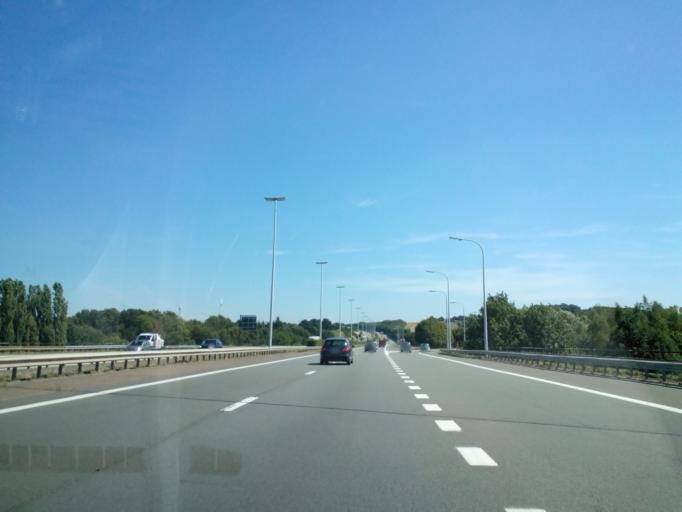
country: BE
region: Flanders
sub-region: Provincie Vlaams-Brabant
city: Bekkevoort
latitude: 50.9530
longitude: 4.9990
